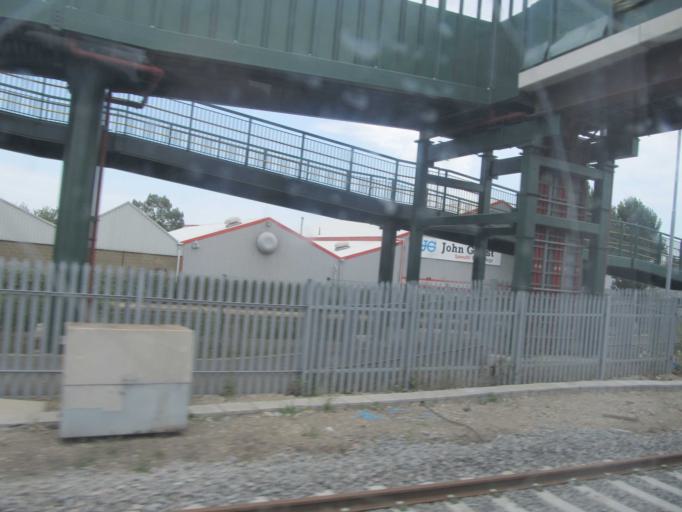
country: GB
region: England
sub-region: Greater London
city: West Drayton
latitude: 51.5095
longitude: -0.4663
